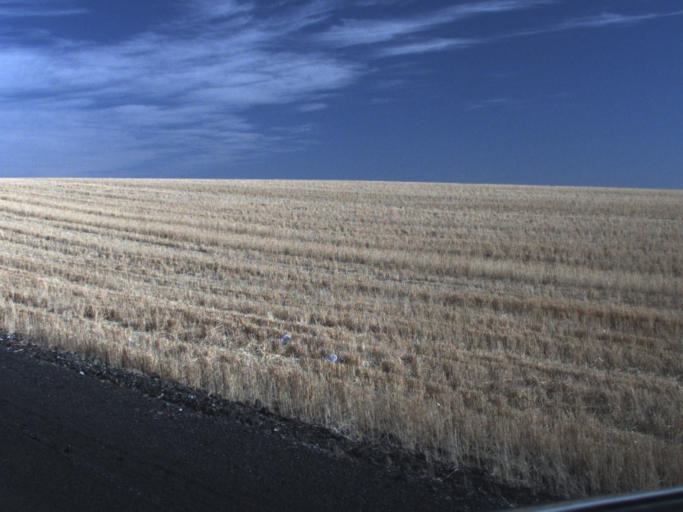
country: US
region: Washington
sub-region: Adams County
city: Ritzville
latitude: 47.1956
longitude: -118.6868
